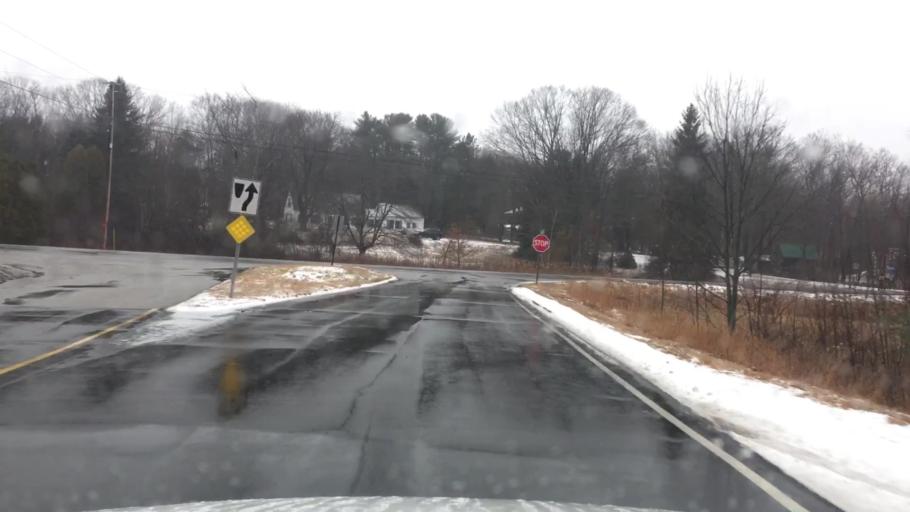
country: US
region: Maine
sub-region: York County
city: Arundel
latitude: 43.4128
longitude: -70.4144
